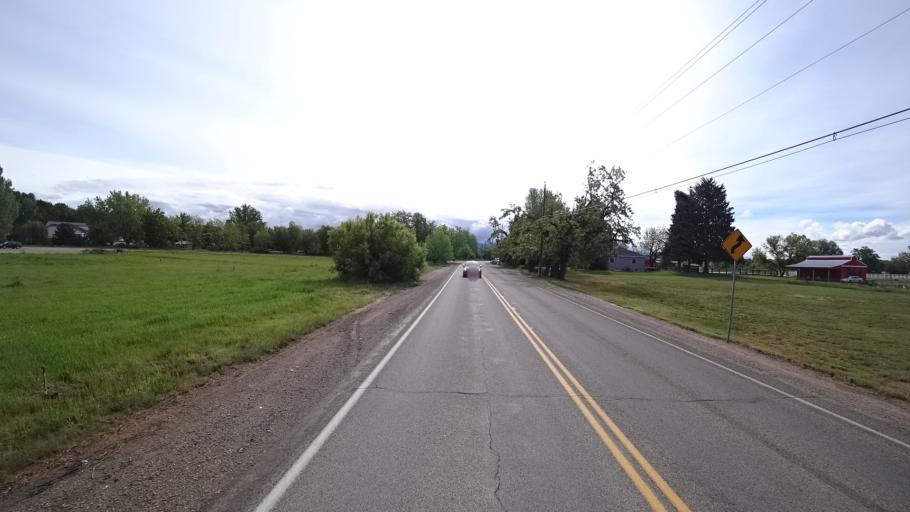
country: US
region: Idaho
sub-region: Ada County
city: Eagle
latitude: 43.7208
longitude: -116.3413
